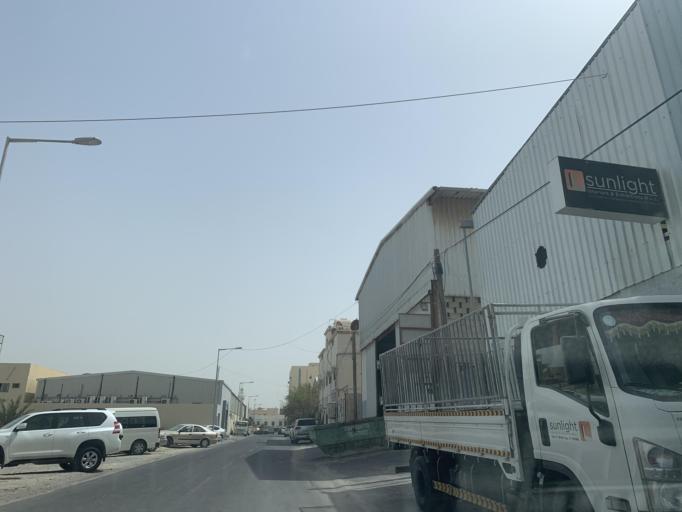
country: BH
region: Northern
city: Madinat `Isa
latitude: 26.1870
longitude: 50.5247
